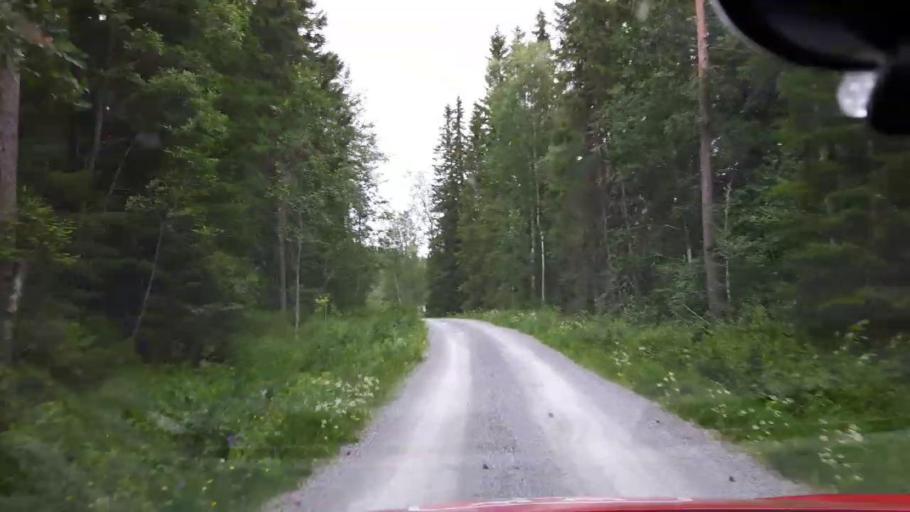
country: SE
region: Jaemtland
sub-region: OEstersunds Kommun
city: Brunflo
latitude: 63.0342
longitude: 14.9290
